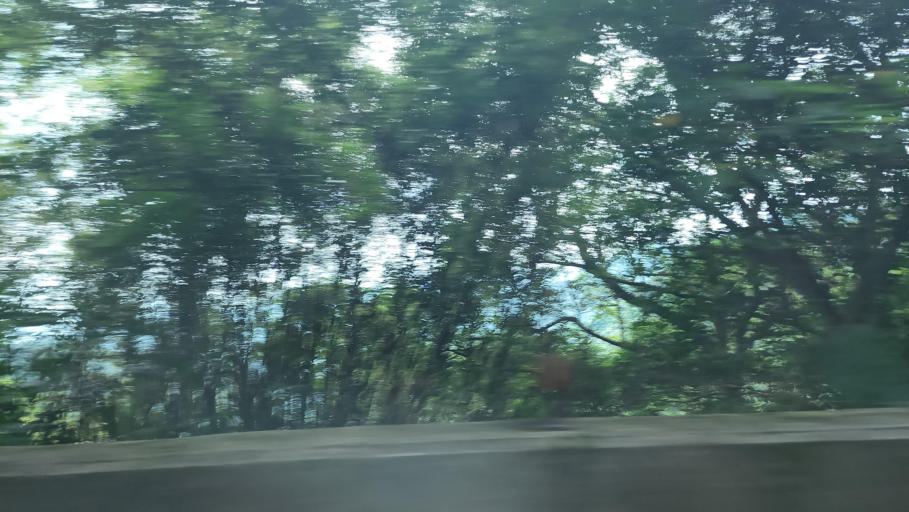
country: TW
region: Taipei
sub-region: Taipei
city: Banqiao
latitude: 24.8898
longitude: 121.4275
